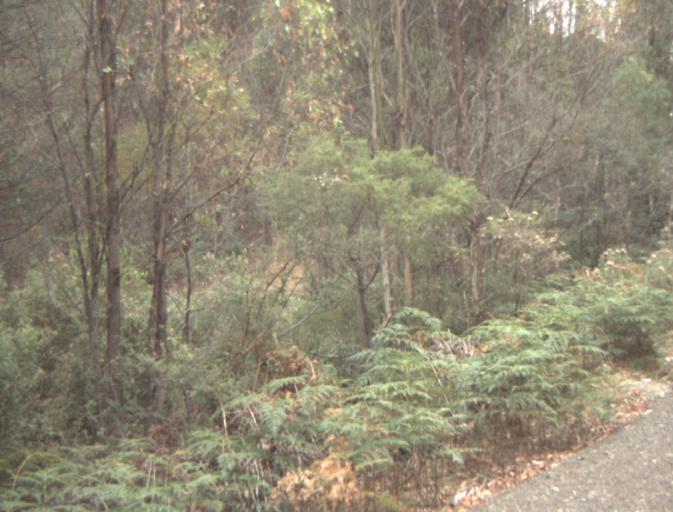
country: AU
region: Tasmania
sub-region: Launceston
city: Mayfield
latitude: -41.2138
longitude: 147.1777
